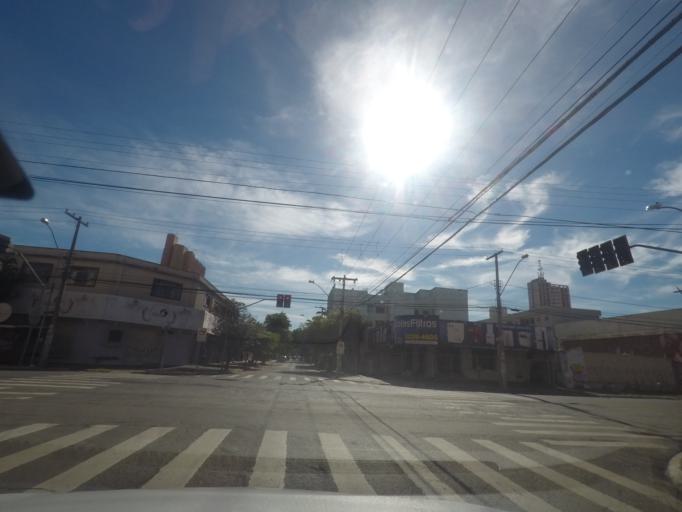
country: BR
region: Goias
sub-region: Goiania
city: Goiania
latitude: -16.6692
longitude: -49.2622
